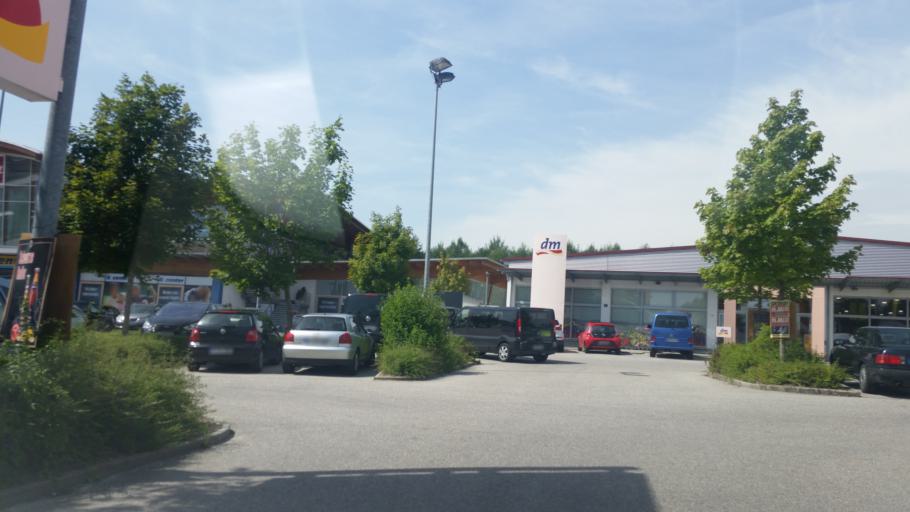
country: DE
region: Bavaria
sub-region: Lower Bavaria
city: Vilsbiburg
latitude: 48.4530
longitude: 12.3349
